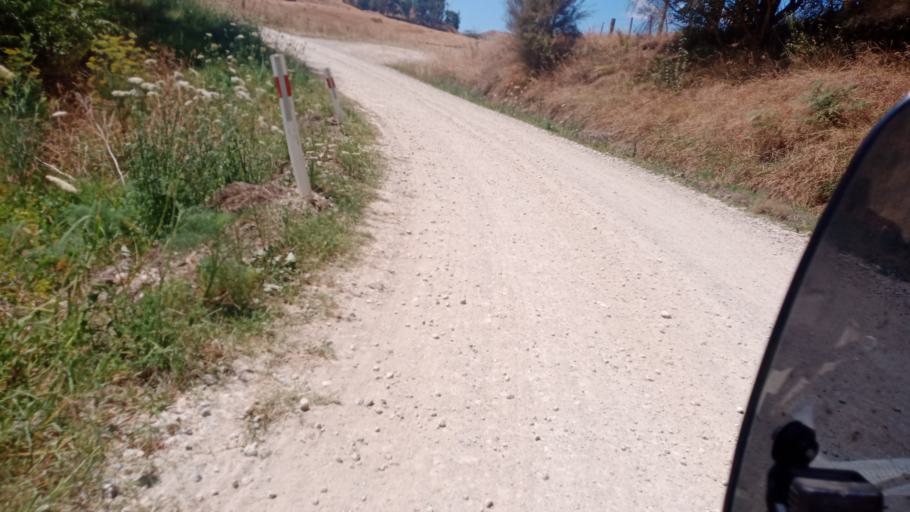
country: NZ
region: Gisborne
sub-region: Gisborne District
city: Gisborne
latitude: -38.5365
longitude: 177.6120
